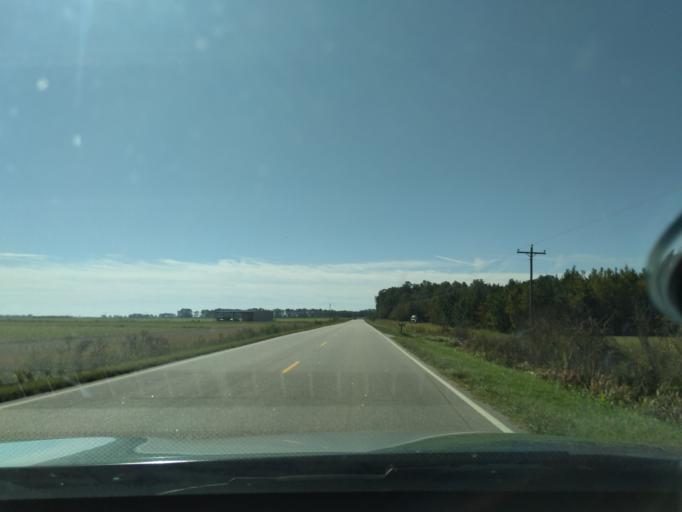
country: US
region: North Carolina
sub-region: Washington County
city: Plymouth
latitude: 35.7503
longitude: -76.7395
